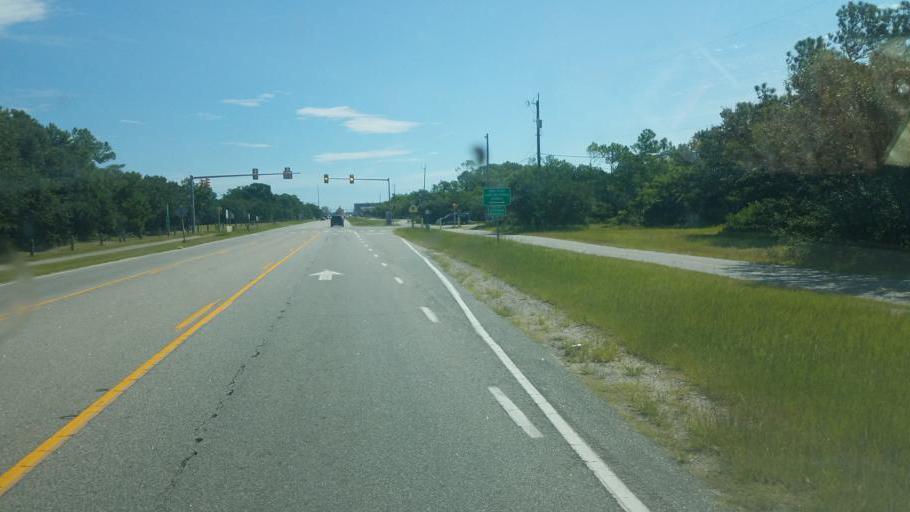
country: US
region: North Carolina
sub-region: Dare County
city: Kill Devil Hills
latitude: 36.0109
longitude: -75.6669
